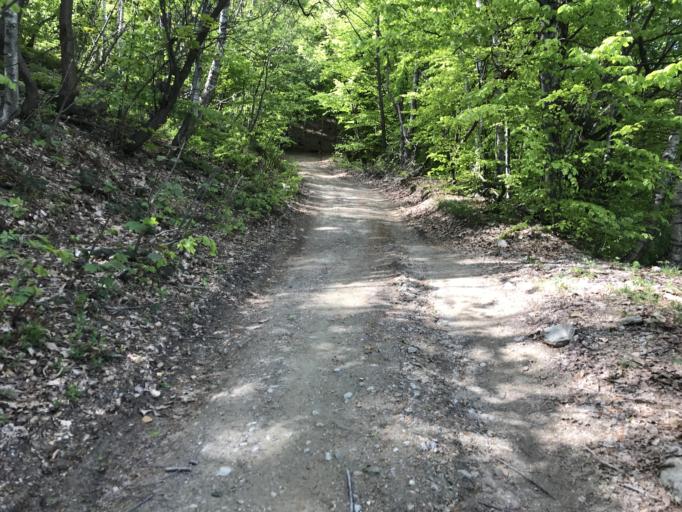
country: IT
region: Piedmont
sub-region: Provincia di Cuneo
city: Robilante
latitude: 44.2940
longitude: 7.5483
